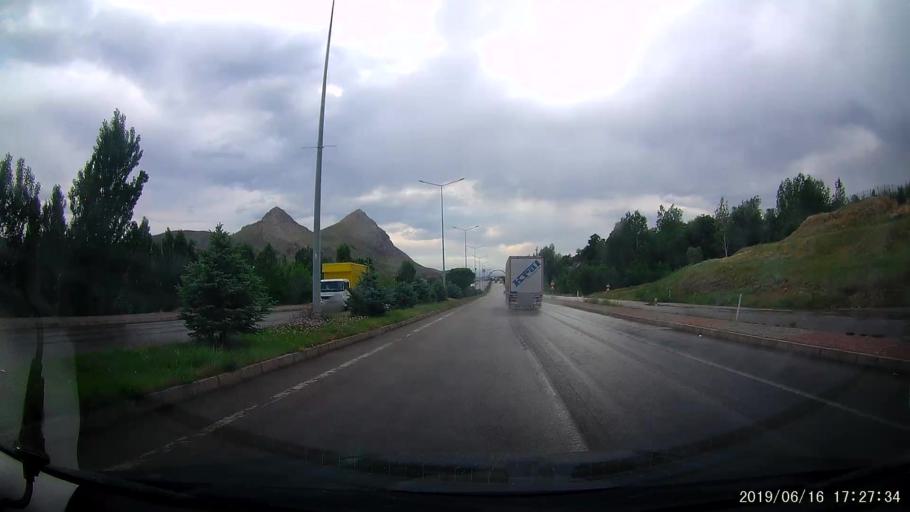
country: TR
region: Erzincan
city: Tercan
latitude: 39.7767
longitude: 40.3912
